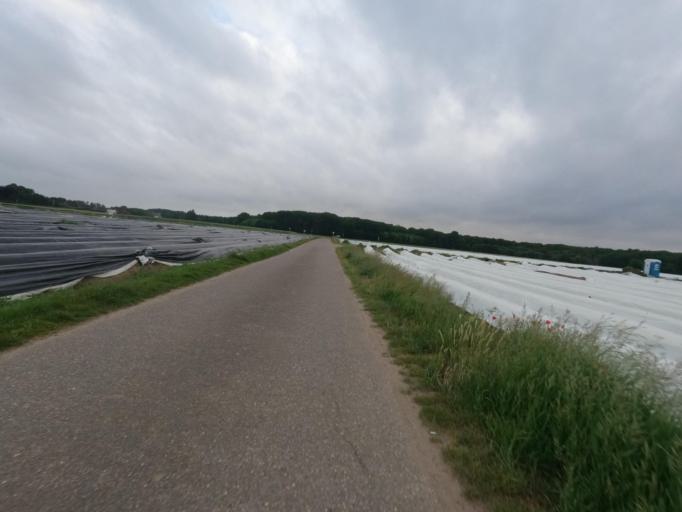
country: NL
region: Limburg
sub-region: Gemeente Roerdalen
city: Vlodrop
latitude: 51.1260
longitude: 6.1131
